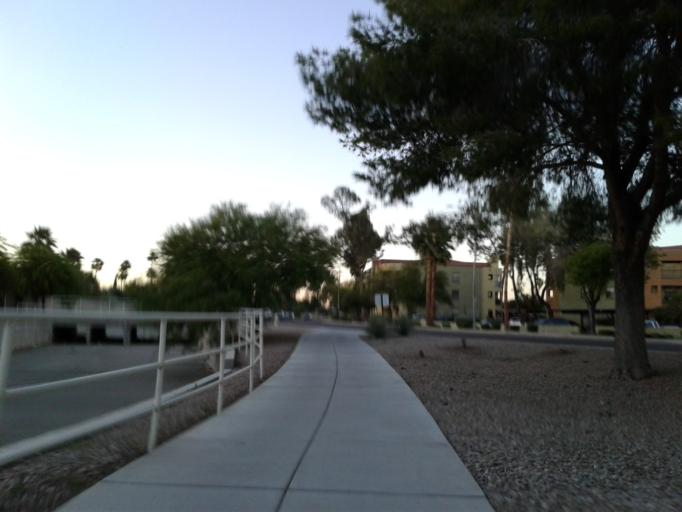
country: US
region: Arizona
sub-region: Maricopa County
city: Paradise Valley
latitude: 33.5990
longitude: -111.9926
